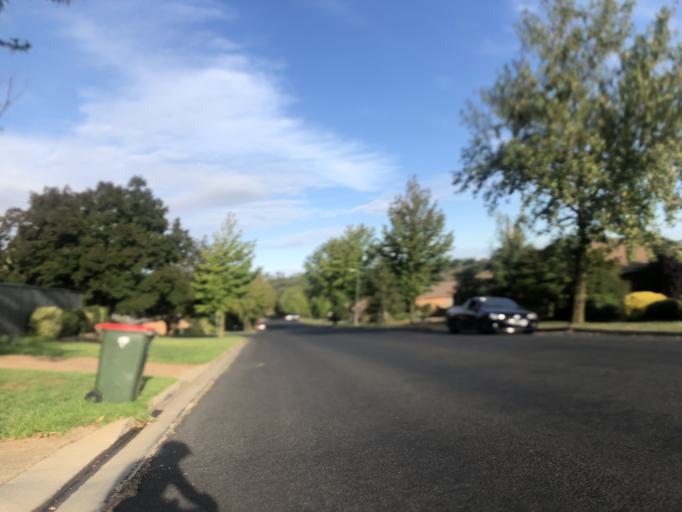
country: AU
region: New South Wales
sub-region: Orange Municipality
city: Orange
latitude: -33.3029
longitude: 149.0945
